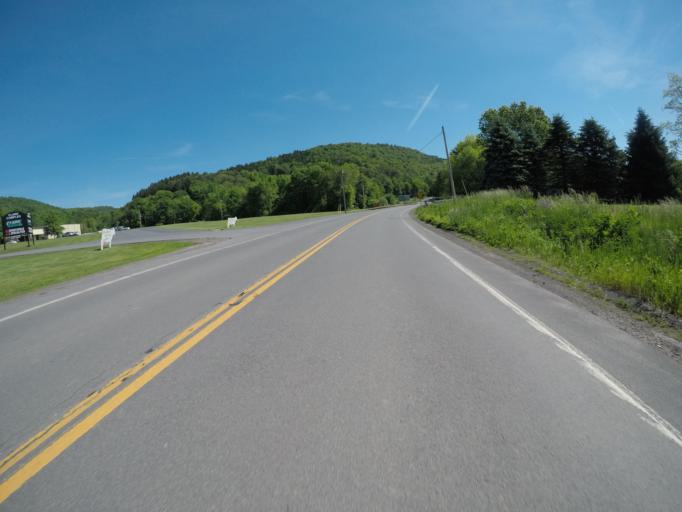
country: US
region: New York
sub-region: Delaware County
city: Delhi
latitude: 42.2565
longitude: -74.9574
